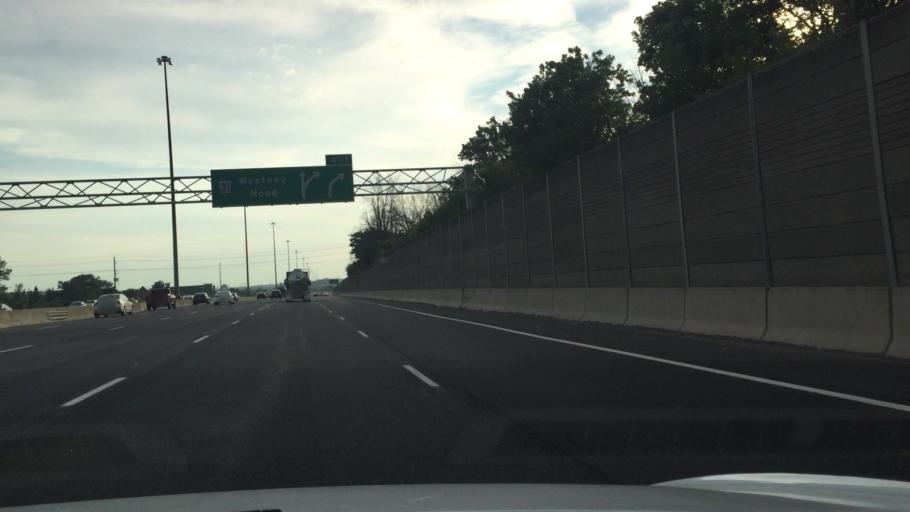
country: CA
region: Ontario
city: Ajax
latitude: 43.8518
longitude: -79.0293
